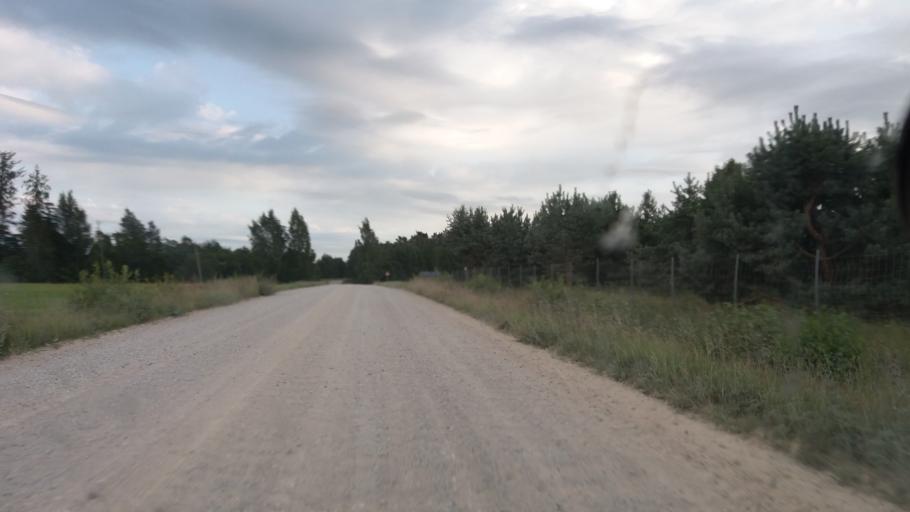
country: LV
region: Talsu Rajons
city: Sabile
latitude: 57.0240
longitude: 22.5862
